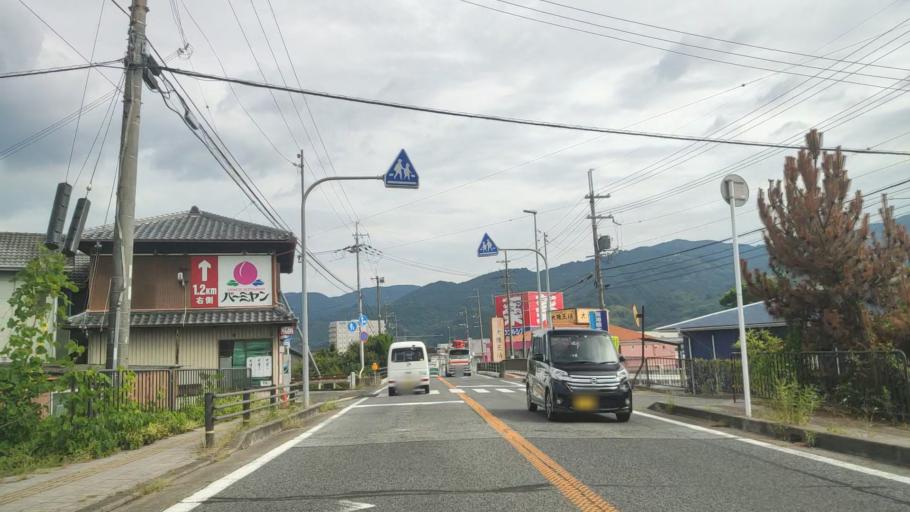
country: JP
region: Wakayama
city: Hashimoto
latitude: 34.3149
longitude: 135.5964
